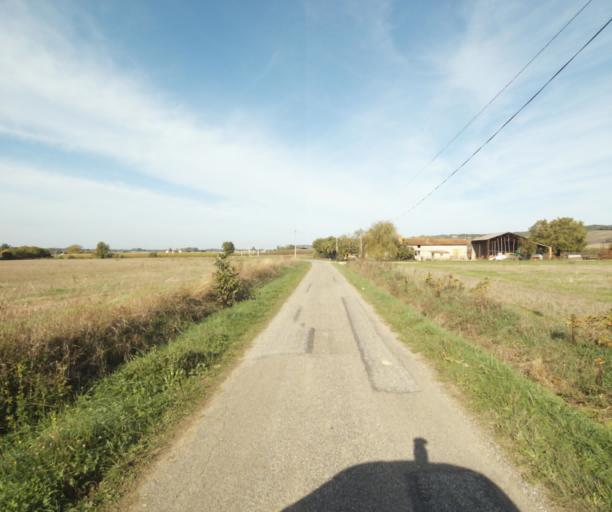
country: FR
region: Midi-Pyrenees
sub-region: Departement du Tarn-et-Garonne
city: Nohic
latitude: 43.9137
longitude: 1.4377
